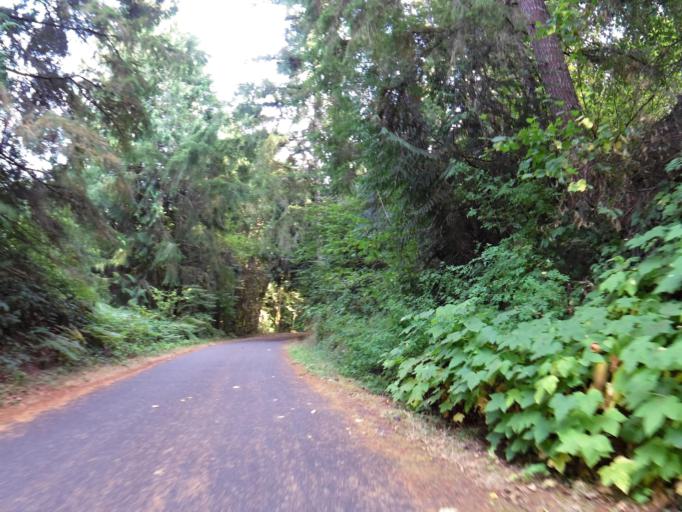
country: US
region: Washington
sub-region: Thurston County
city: Lacey
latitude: 46.9785
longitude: -122.8143
